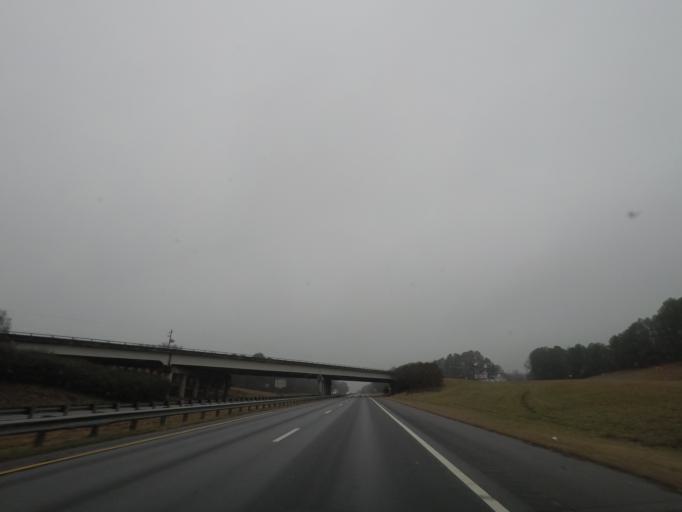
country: US
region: North Carolina
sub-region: Chatham County
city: Farmville
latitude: 35.6165
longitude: -79.0977
